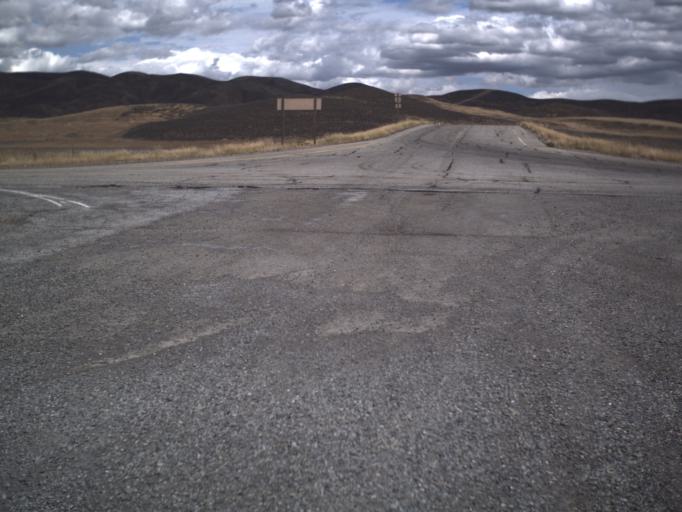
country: US
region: Utah
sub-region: Box Elder County
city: Garland
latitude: 41.8400
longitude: -112.4397
